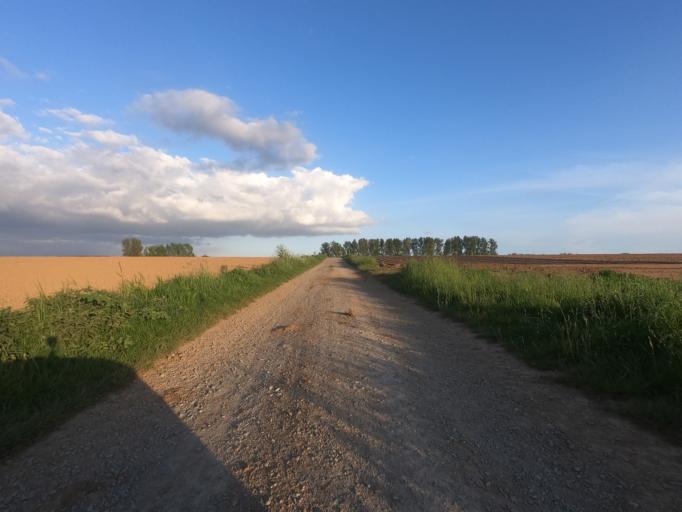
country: BE
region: Flanders
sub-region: Provincie Vlaams-Brabant
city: Gooik
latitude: 50.7788
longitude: 4.1362
